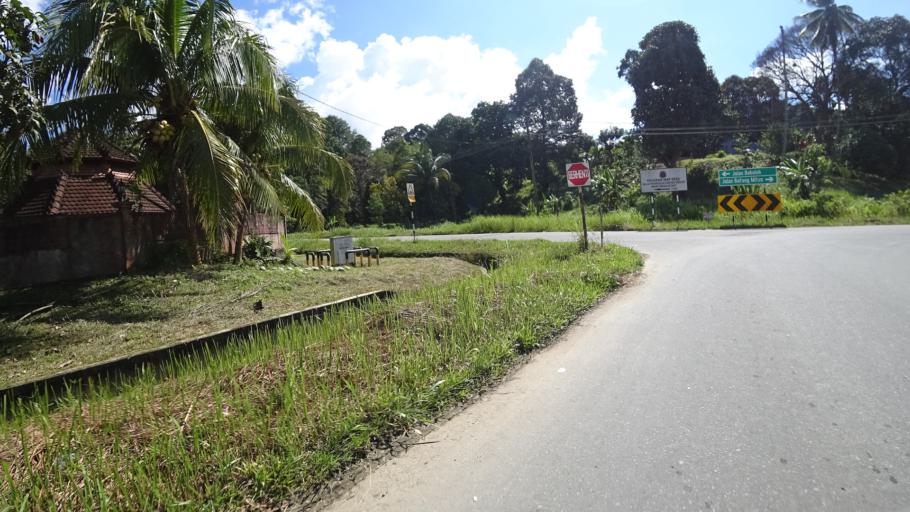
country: BN
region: Tutong
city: Tutong
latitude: 4.7506
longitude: 114.7832
